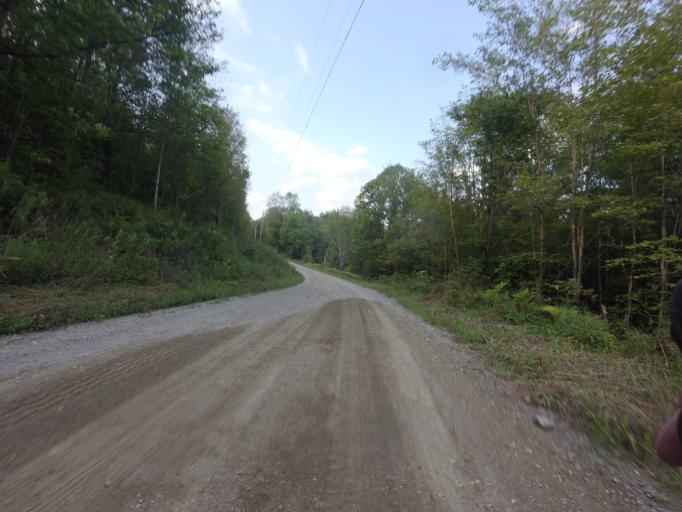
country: CA
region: Ontario
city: Perth
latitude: 44.8387
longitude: -76.7192
